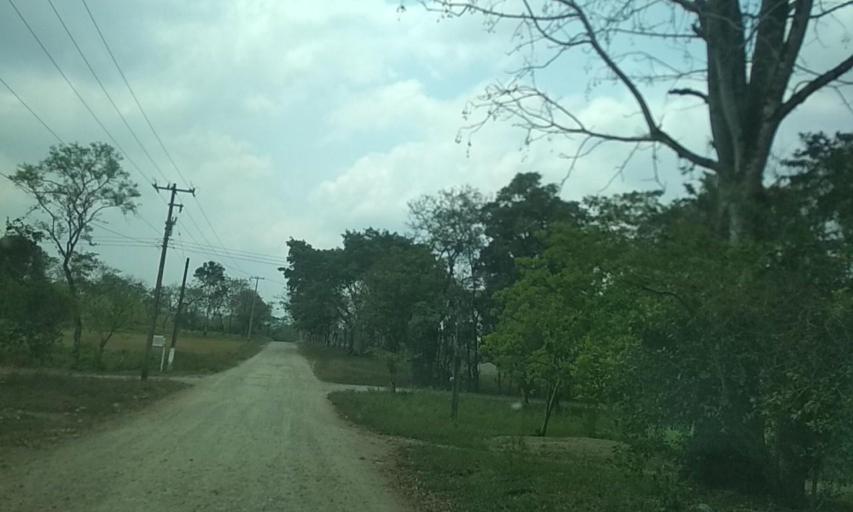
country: MX
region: Tabasco
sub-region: Huimanguillo
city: Francisco Rueda
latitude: 17.5999
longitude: -93.7967
